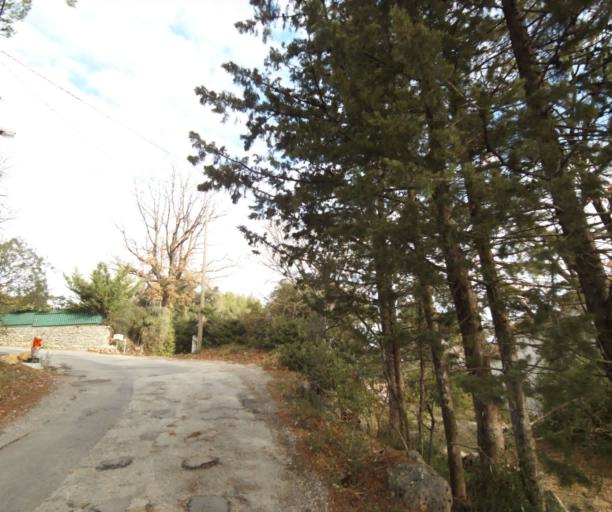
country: FR
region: Provence-Alpes-Cote d'Azur
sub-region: Departement du Var
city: Trans-en-Provence
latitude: 43.5028
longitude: 6.4810
